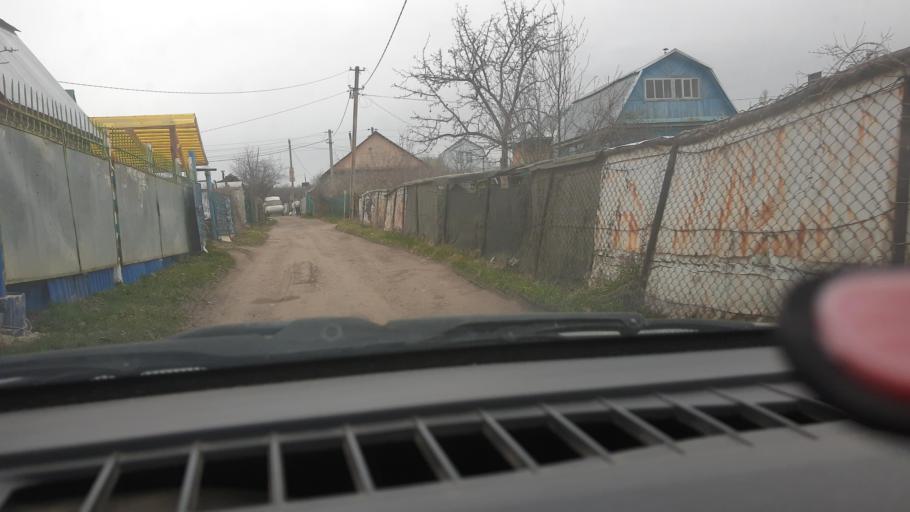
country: RU
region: Bashkortostan
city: Mikhaylovka
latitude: 54.9231
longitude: 55.8835
